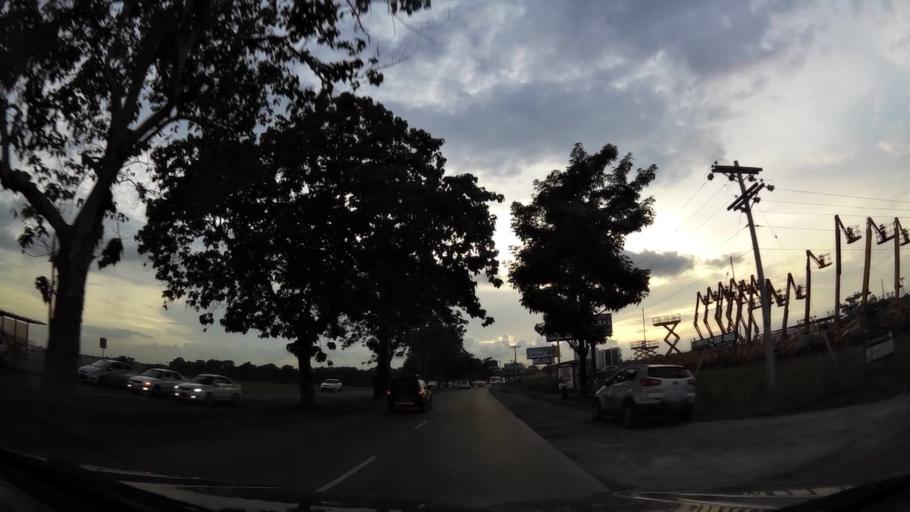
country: PA
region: Panama
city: Tocumen
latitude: 9.0704
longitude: -79.3901
